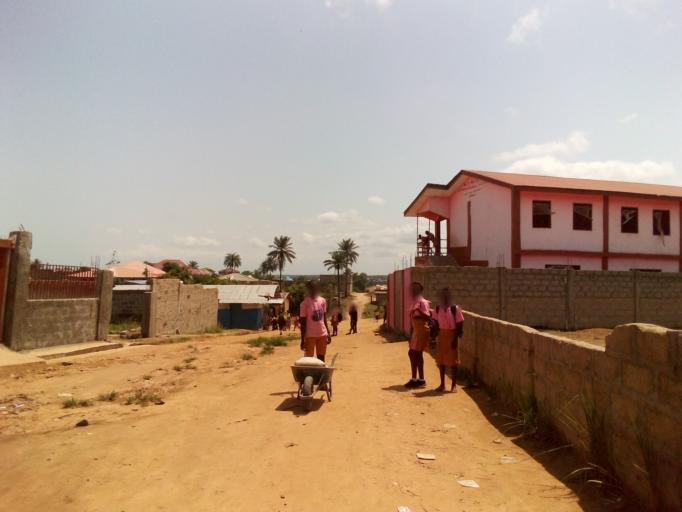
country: SL
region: Western Area
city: Waterloo
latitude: 8.3389
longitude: -13.0296
